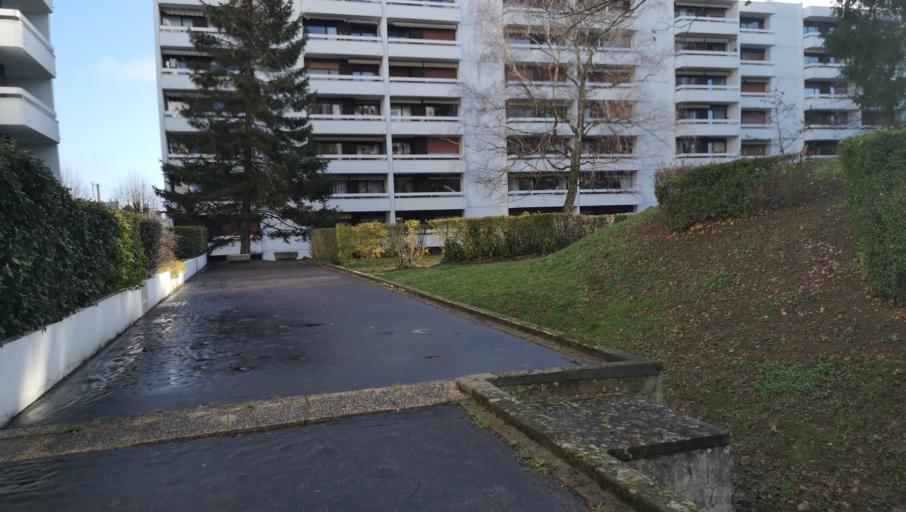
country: FR
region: Centre
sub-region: Departement du Loiret
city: Orleans
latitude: 47.9019
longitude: 1.8865
